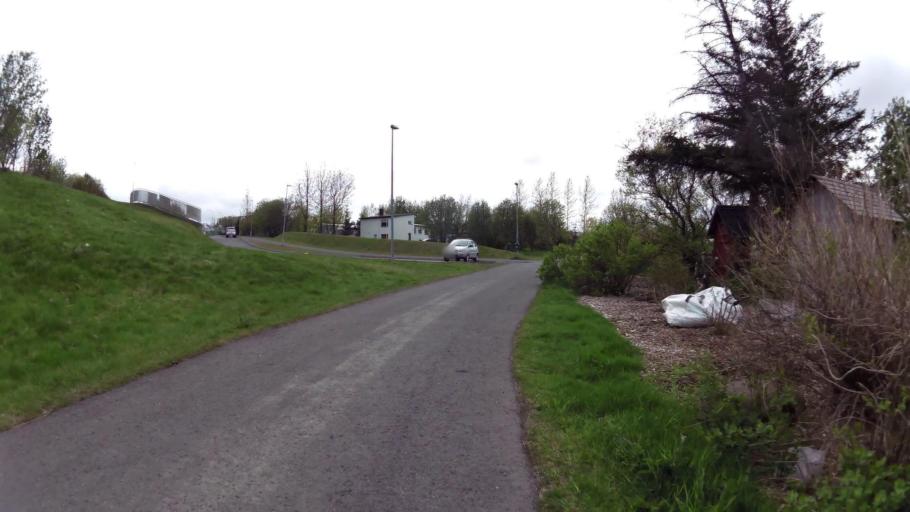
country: IS
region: Capital Region
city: Reykjavik
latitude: 64.1149
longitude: -21.8456
